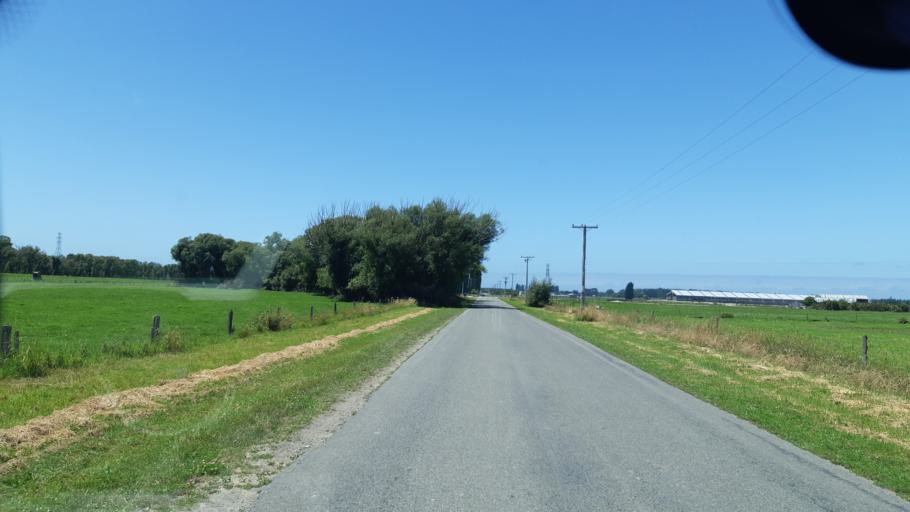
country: NZ
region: Canterbury
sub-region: Waimakariri District
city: Woodend
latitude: -43.2797
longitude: 172.6494
